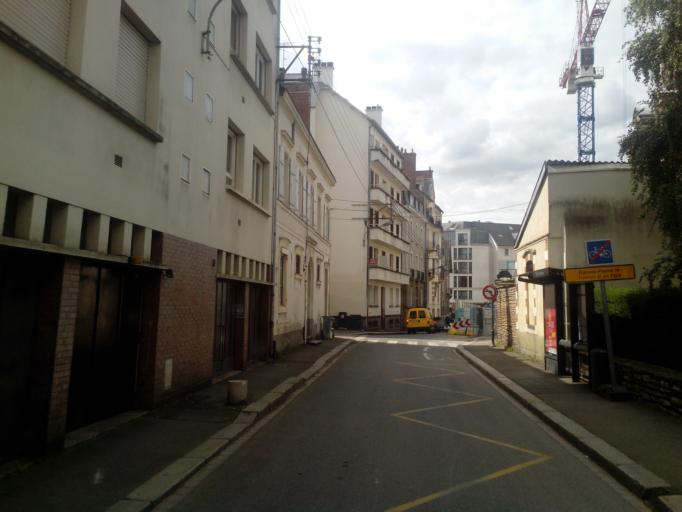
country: FR
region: Brittany
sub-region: Departement d'Ille-et-Vilaine
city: Rennes
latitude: 48.1180
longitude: -1.6750
